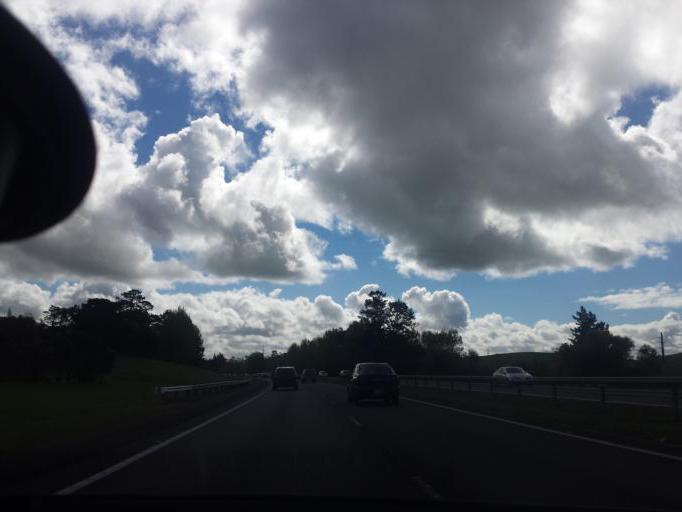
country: NZ
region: Auckland
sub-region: Auckland
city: Rothesay Bay
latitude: -36.6701
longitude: 174.6812
